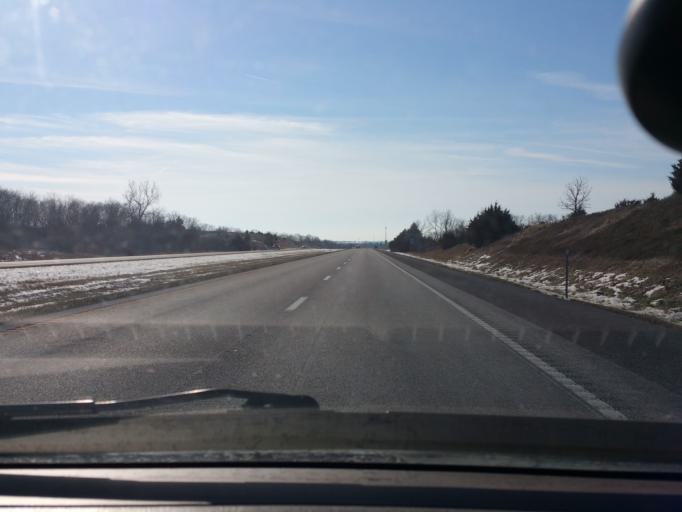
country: US
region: Missouri
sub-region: Clinton County
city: Cameron
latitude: 39.8948
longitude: -94.1541
